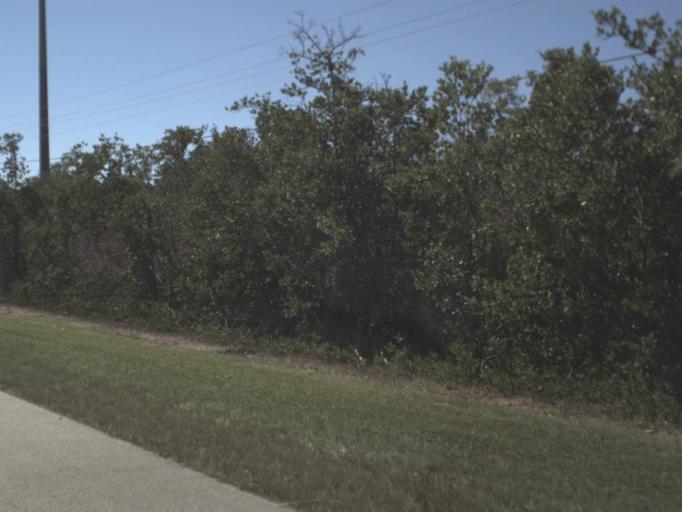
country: US
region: Florida
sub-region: Collier County
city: Marco
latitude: 25.9927
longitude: -81.7021
